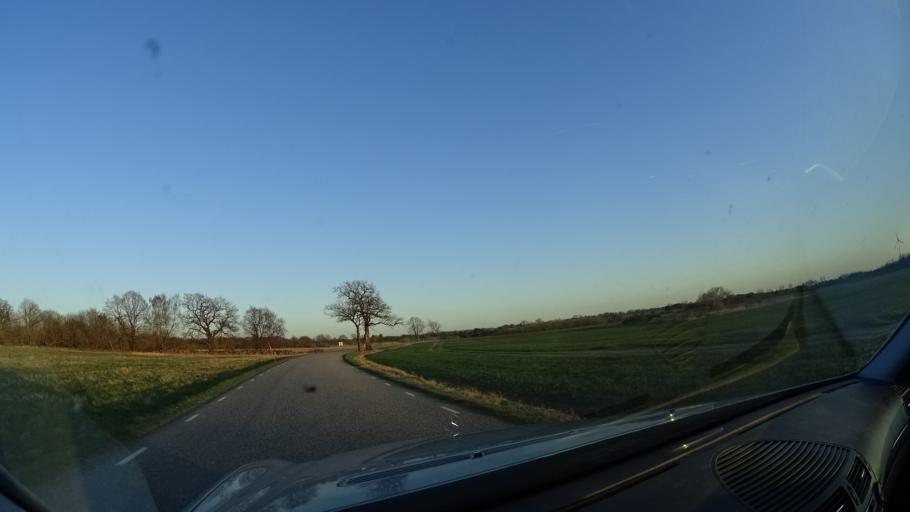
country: SE
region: Skane
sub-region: Hoors Kommun
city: Loberod
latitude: 55.8377
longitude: 13.4578
